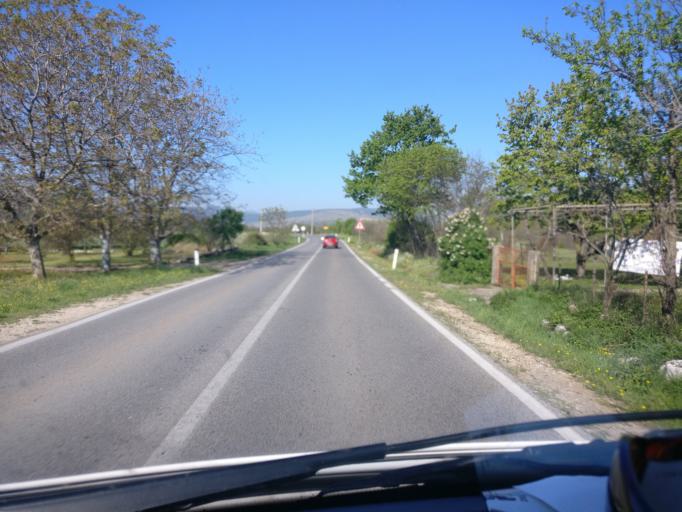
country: BA
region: Federation of Bosnia and Herzegovina
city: Tasovcici
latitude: 43.1267
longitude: 17.7603
